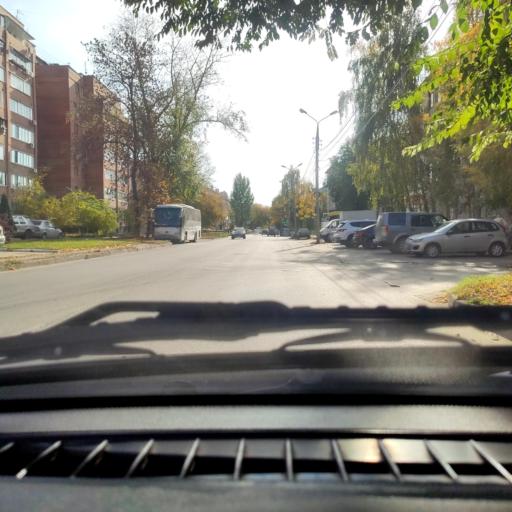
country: RU
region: Samara
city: Tol'yatti
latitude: 53.5086
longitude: 49.4067
